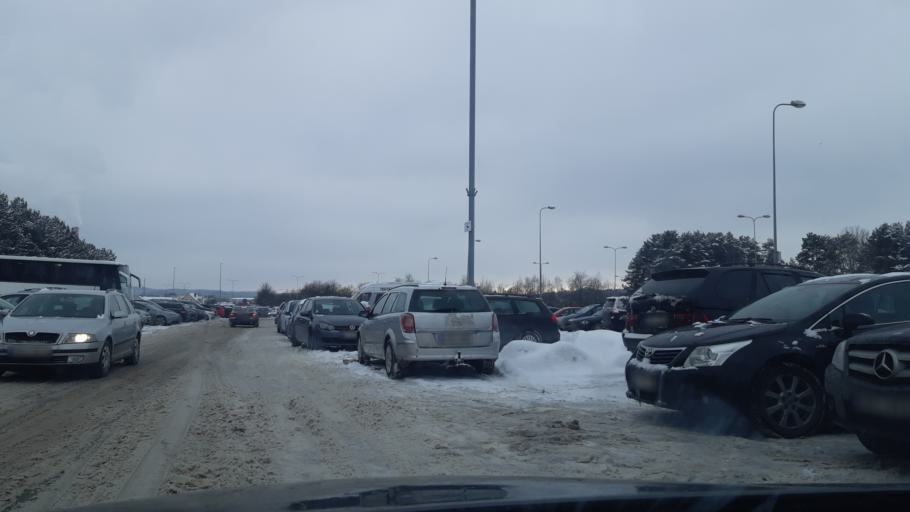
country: LT
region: Vilnius County
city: Vilkpede
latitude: 54.6779
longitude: 25.2272
